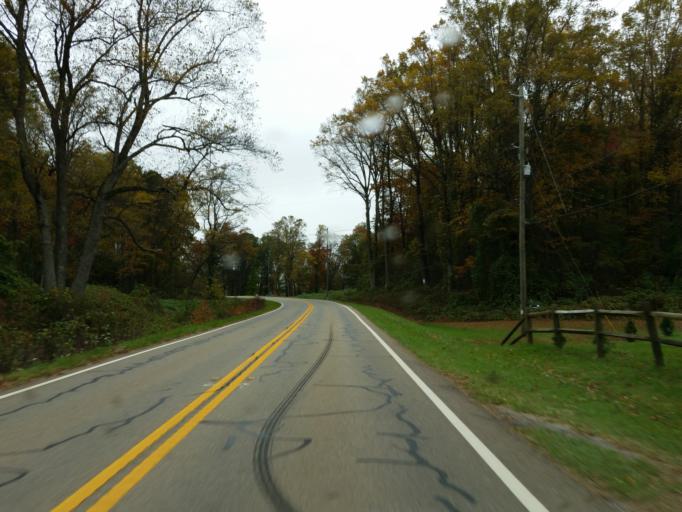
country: US
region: Georgia
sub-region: Pickens County
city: Jasper
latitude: 34.5295
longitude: -84.4011
